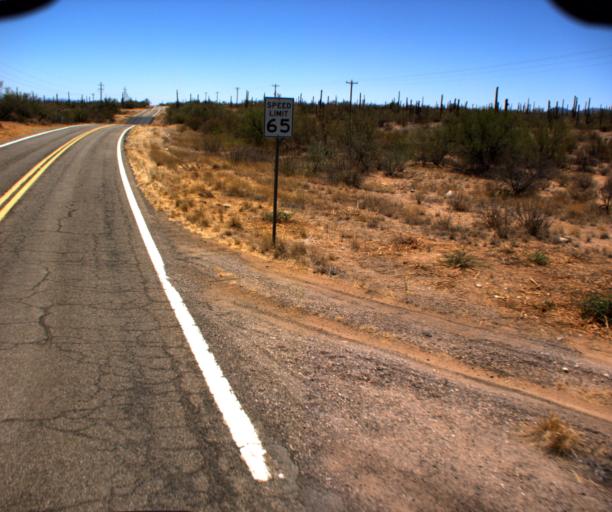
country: US
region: Arizona
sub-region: Pima County
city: Sells
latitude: 32.1563
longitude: -112.1083
